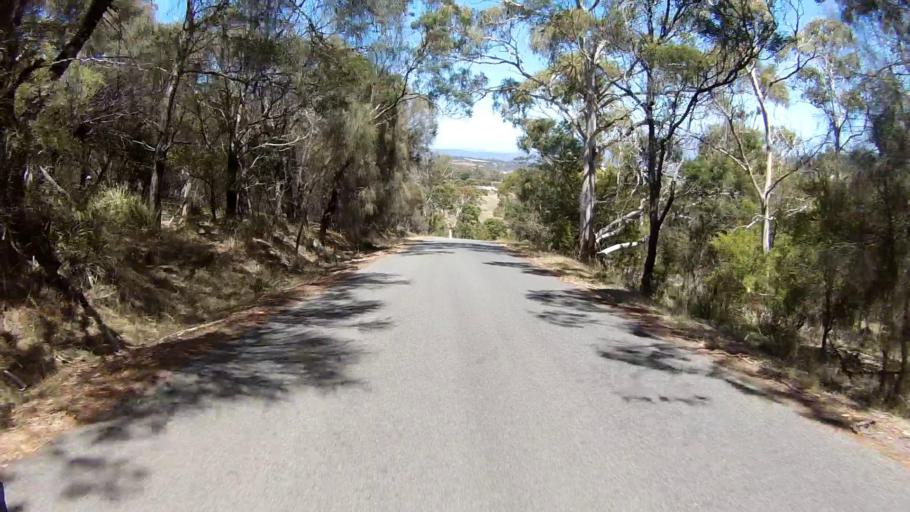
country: AU
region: Tasmania
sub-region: Clarence
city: Cambridge
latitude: -42.8501
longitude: 147.4298
